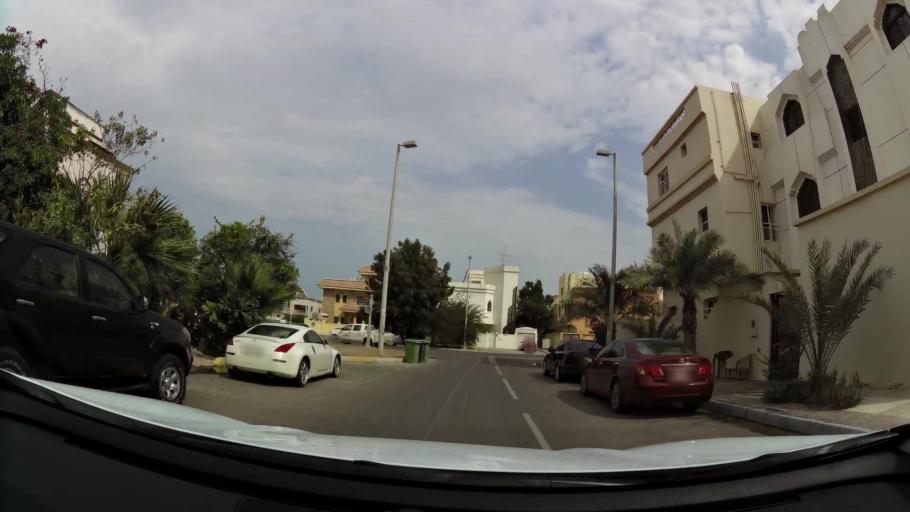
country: AE
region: Abu Dhabi
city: Abu Dhabi
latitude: 24.4402
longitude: 54.4323
